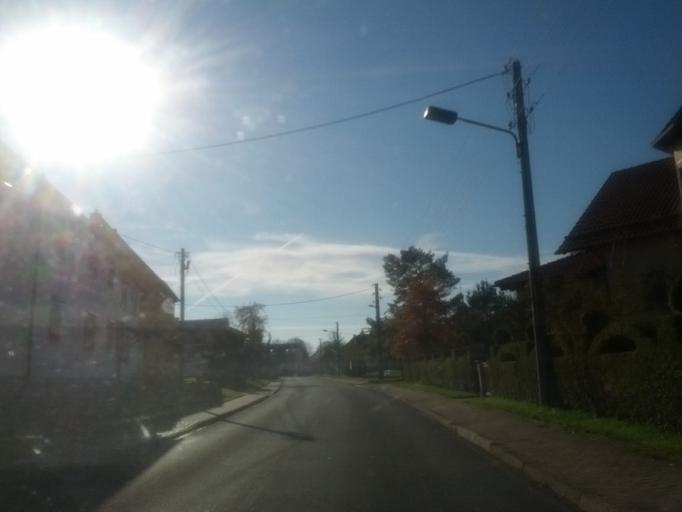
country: DE
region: Thuringia
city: Mechterstadt
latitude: 50.9293
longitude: 10.5460
